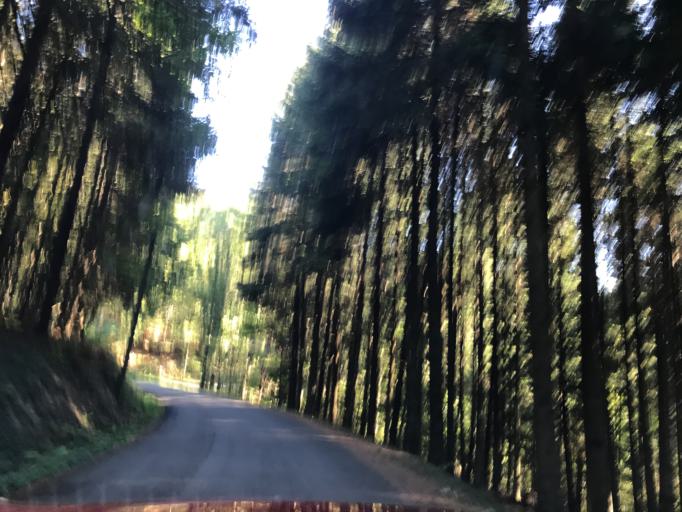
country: FR
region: Auvergne
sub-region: Departement du Puy-de-Dome
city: Escoutoux
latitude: 45.7824
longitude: 3.6075
